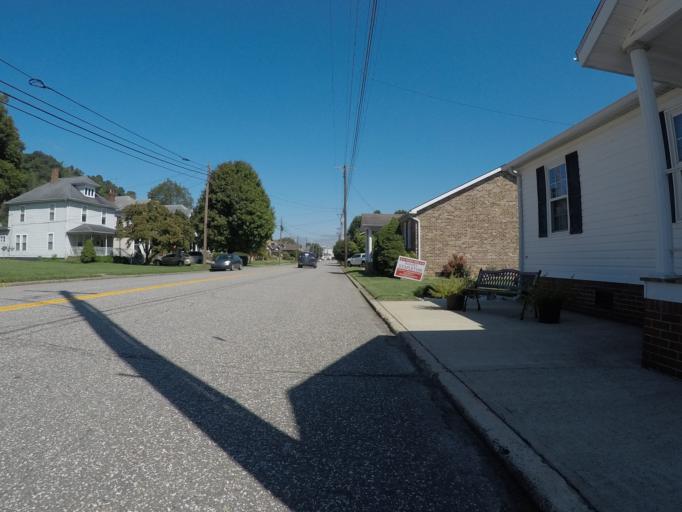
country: US
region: Kentucky
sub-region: Boyd County
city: Catlettsburg
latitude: 38.4100
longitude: -82.5982
